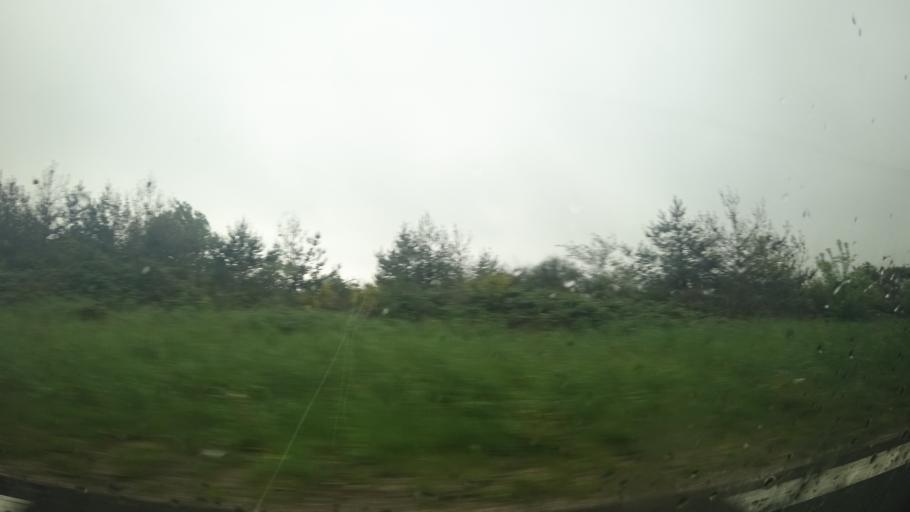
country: FR
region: Midi-Pyrenees
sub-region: Departement de l'Aveyron
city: Severac-le-Chateau
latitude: 44.2267
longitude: 2.9875
